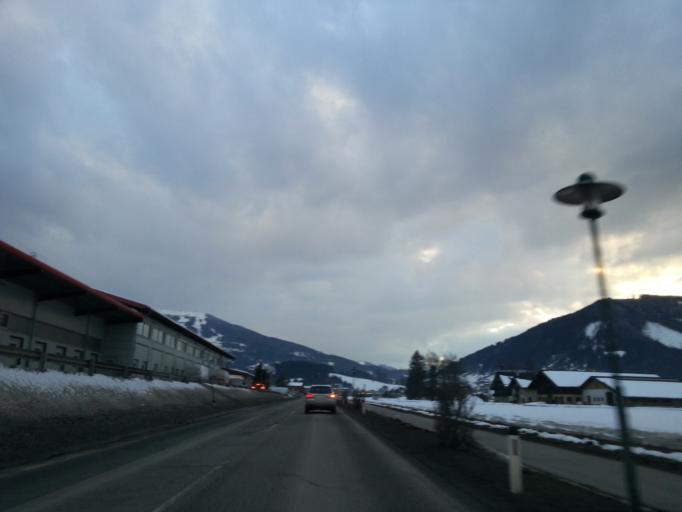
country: AT
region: Salzburg
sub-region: Politischer Bezirk Sankt Johann im Pongau
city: Altenmarkt im Pongau
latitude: 47.3804
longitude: 13.4004
